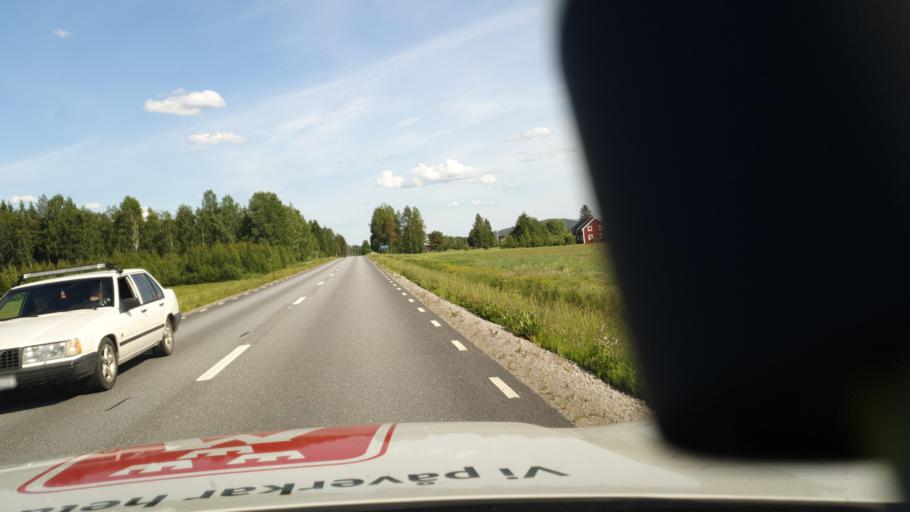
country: SE
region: Vaesterbotten
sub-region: Skelleftea Kommun
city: Forsbacka
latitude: 64.7020
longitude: 20.4561
